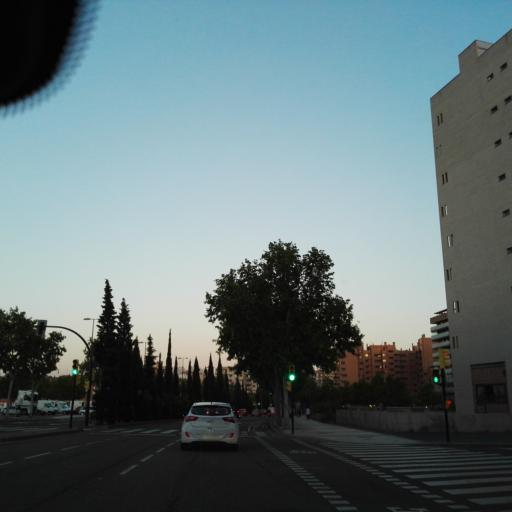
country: ES
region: Aragon
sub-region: Provincia de Zaragoza
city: Zaragoza
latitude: 41.6654
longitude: -0.8685
